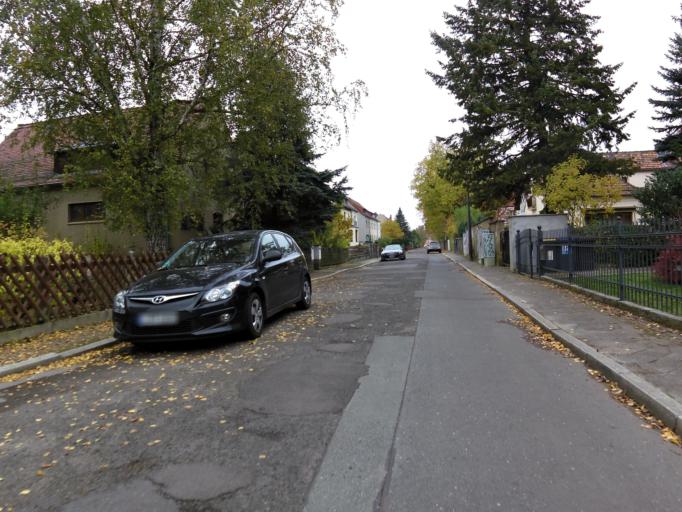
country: DE
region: Saxony
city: Leipzig
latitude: 51.3100
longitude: 12.3676
